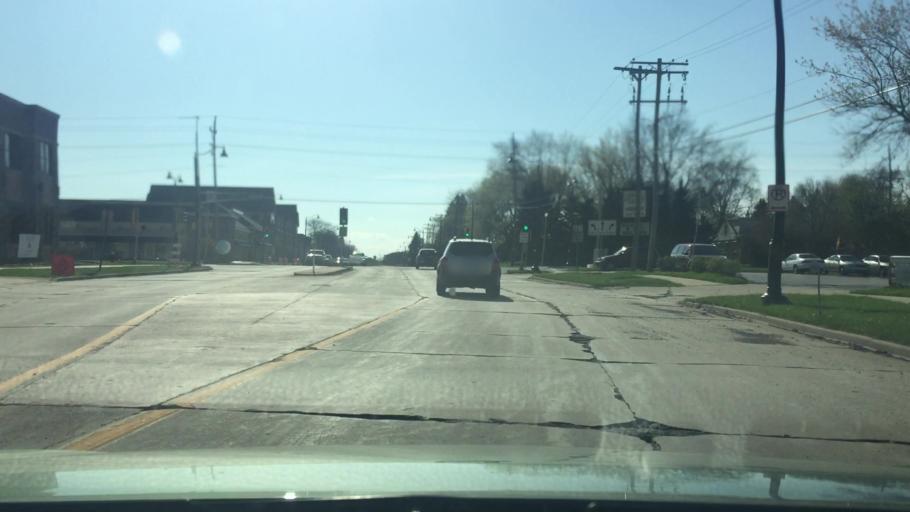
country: US
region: Wisconsin
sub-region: Milwaukee County
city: Brown Deer
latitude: 43.1632
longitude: -87.9638
